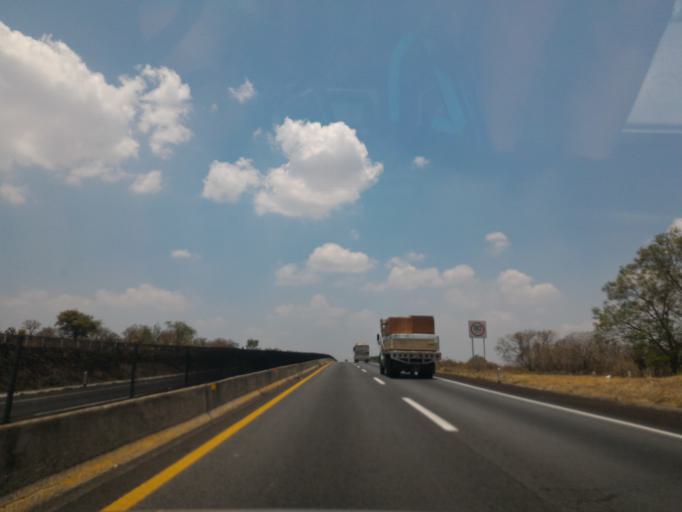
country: MX
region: Jalisco
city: Zapotlanejo
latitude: 20.6864
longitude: -103.0073
